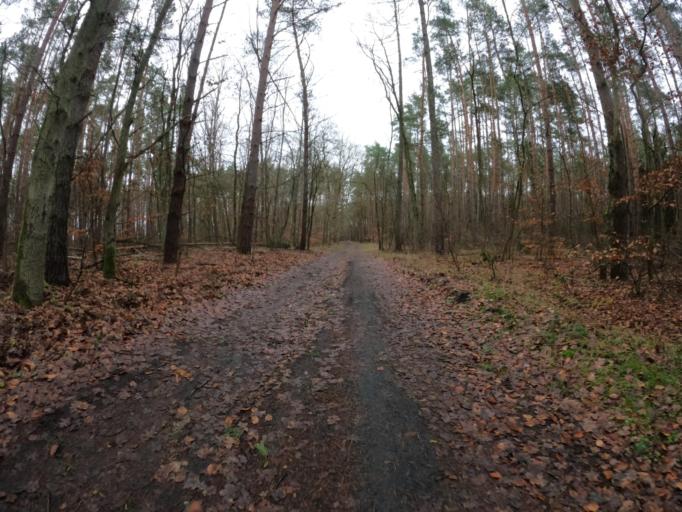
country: PL
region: West Pomeranian Voivodeship
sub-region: Powiat mysliborski
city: Debno
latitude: 52.7390
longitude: 14.7656
